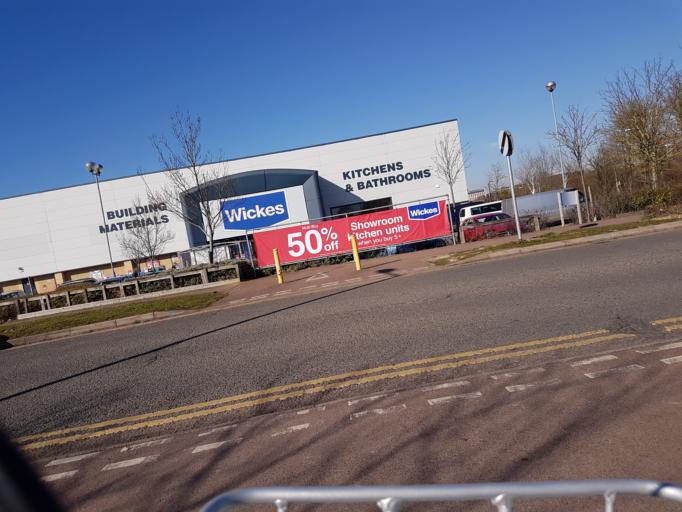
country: GB
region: England
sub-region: Milton Keynes
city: Milton Keynes
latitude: 52.0280
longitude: -0.7618
